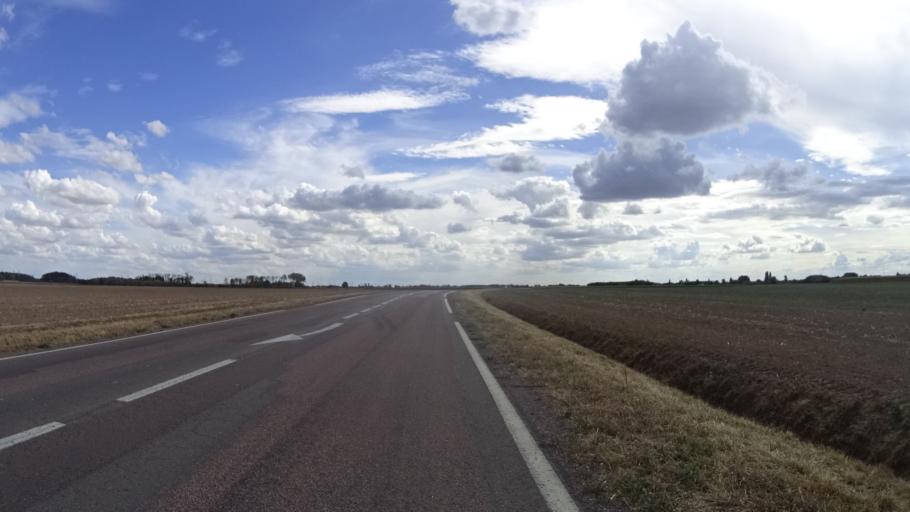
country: FR
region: Bourgogne
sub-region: Departement de la Cote-d'Or
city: Seurre
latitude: 47.0257
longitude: 5.1698
